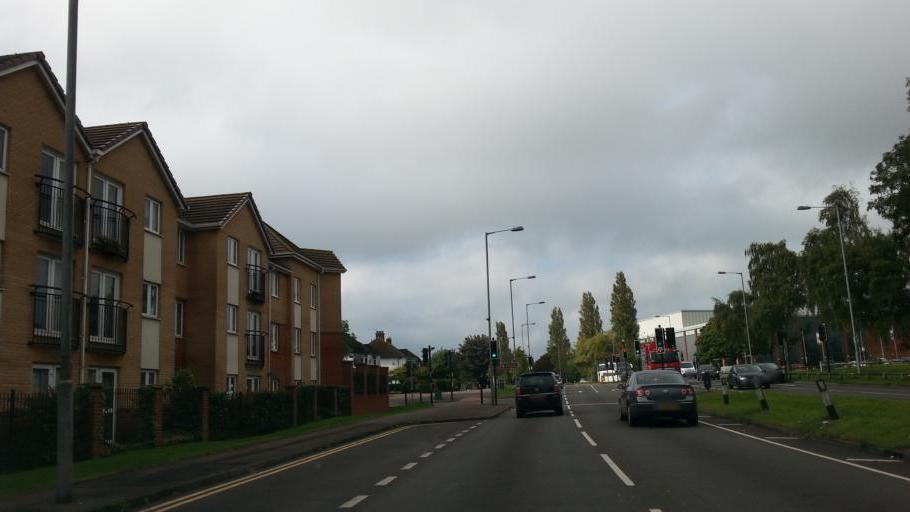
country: GB
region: England
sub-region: Luton
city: Luton
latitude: 51.9067
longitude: -0.3911
